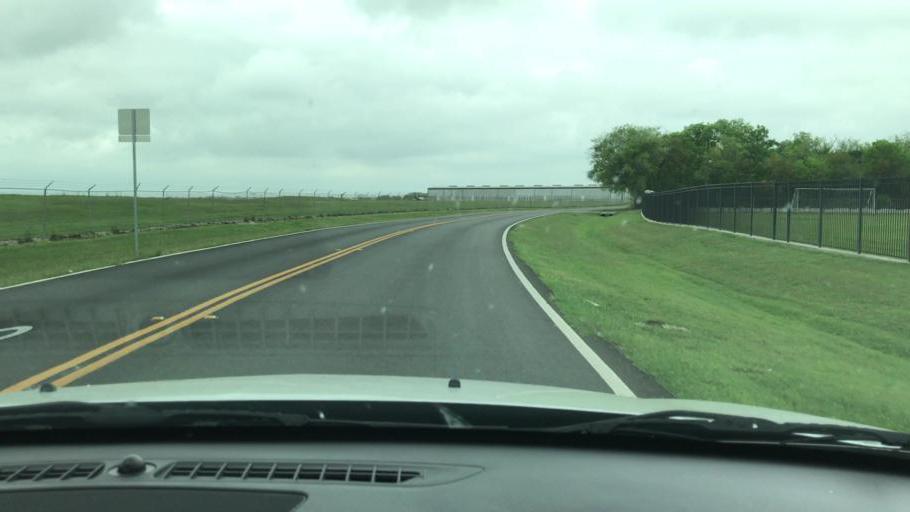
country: US
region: Texas
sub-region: Bexar County
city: San Antonio
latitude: 29.3357
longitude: -98.4637
